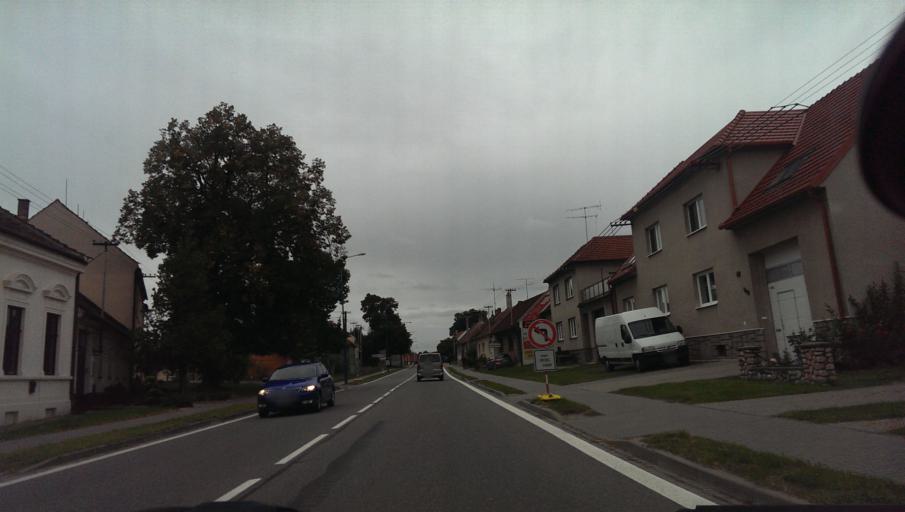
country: CZ
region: South Moravian
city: Bzenec
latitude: 48.9714
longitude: 17.2720
